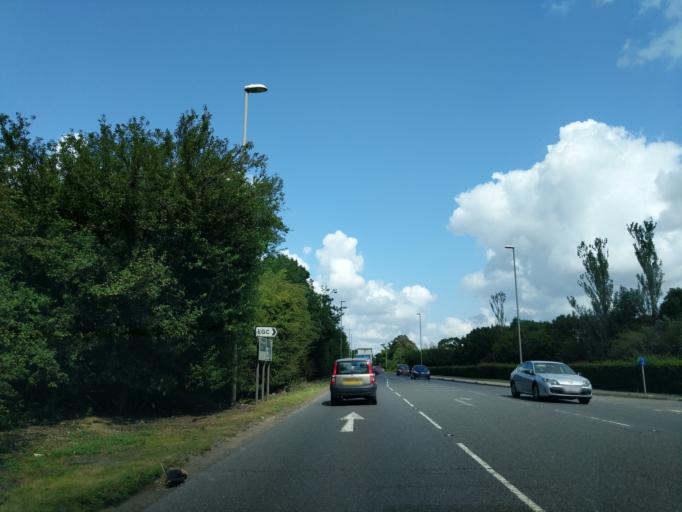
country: GB
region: England
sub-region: Suffolk
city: Exning
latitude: 52.2925
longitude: 0.3905
